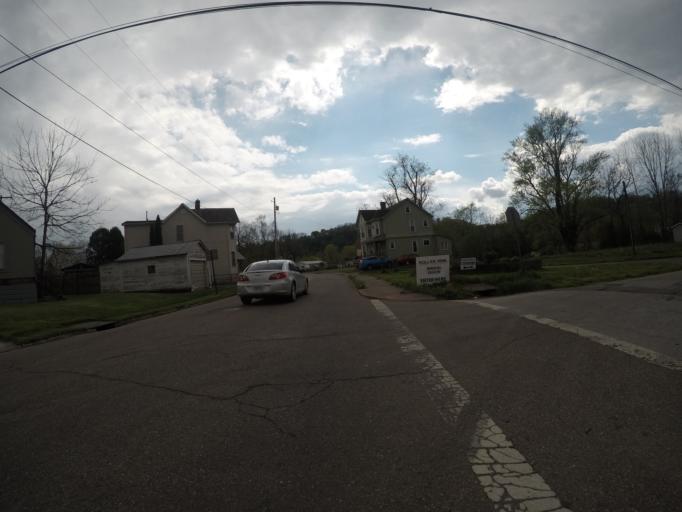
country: US
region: Ohio
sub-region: Washington County
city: Marietta
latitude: 39.4266
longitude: -81.4672
